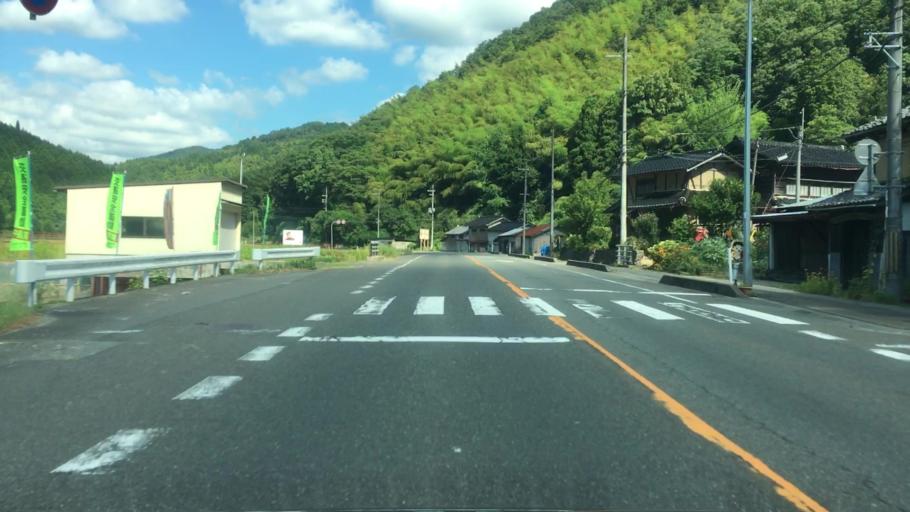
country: JP
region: Hyogo
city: Toyooka
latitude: 35.5708
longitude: 134.7801
